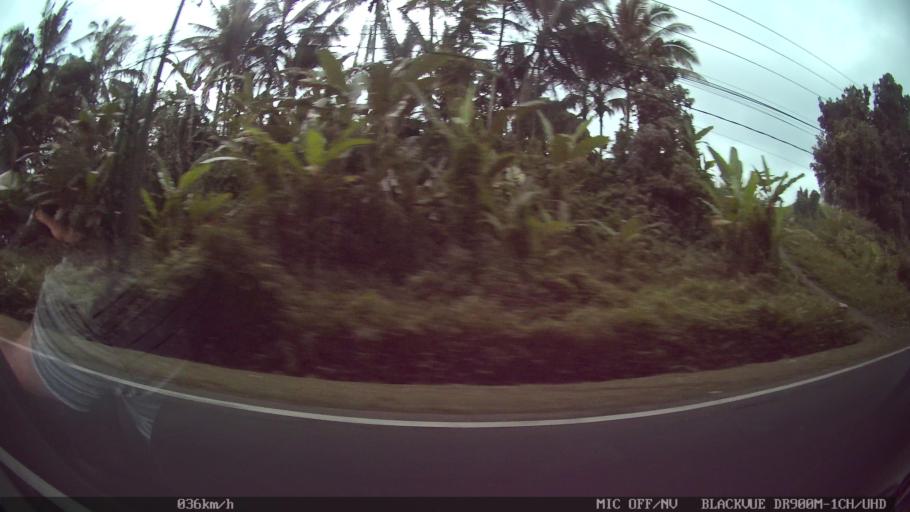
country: ID
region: Bali
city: Penebel
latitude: -8.4144
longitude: 115.1448
